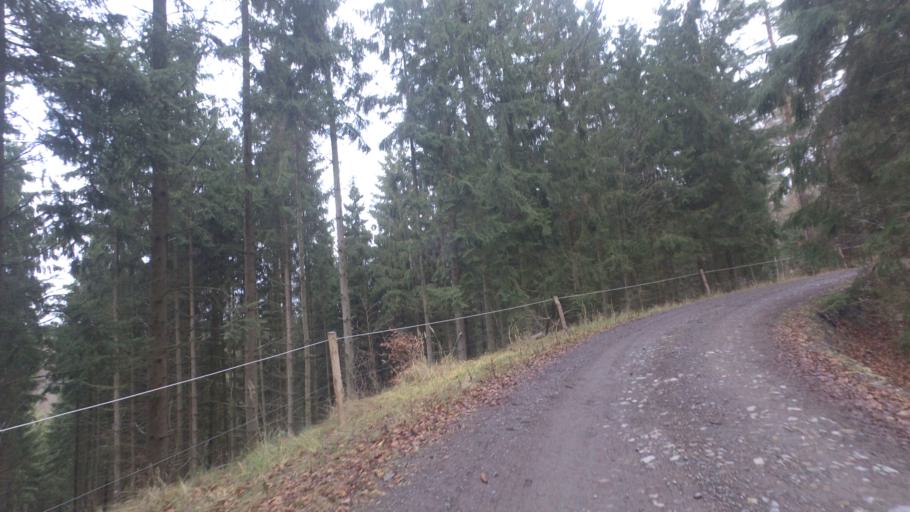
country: DE
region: Thuringia
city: Herschdorf
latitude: 50.7017
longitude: 11.4907
